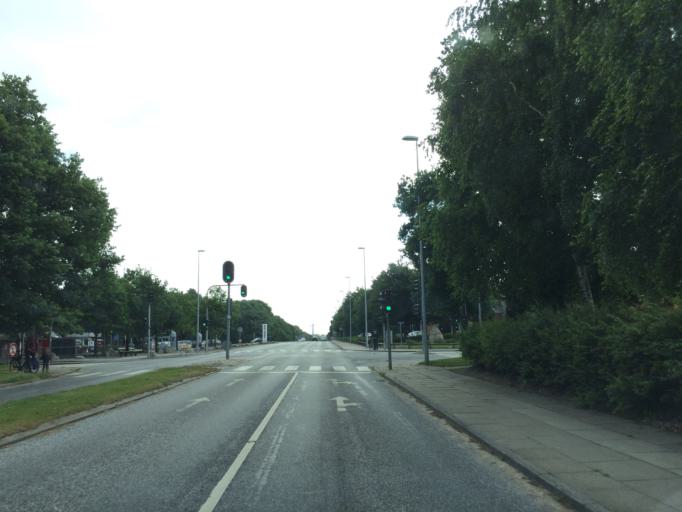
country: DK
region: Central Jutland
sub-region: Herning Kommune
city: Herning
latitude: 56.1454
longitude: 8.9605
